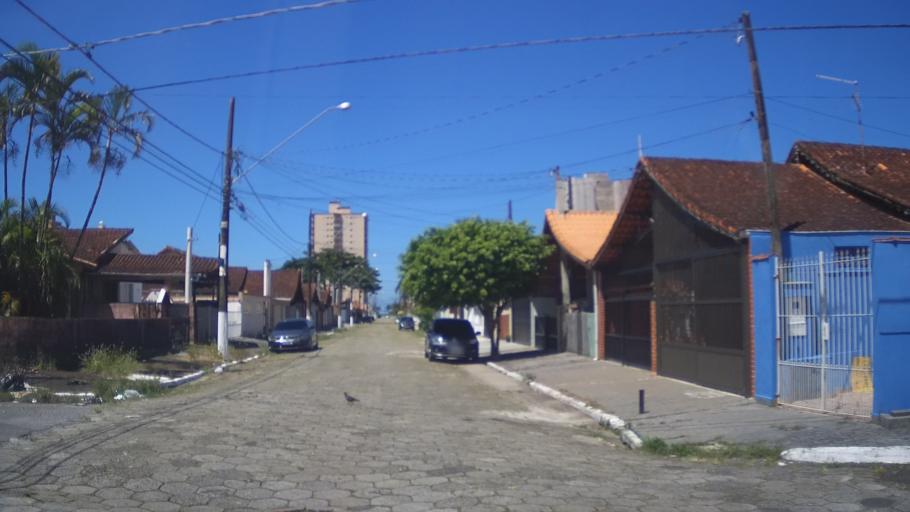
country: BR
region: Sao Paulo
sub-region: Mongagua
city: Mongagua
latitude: -24.0444
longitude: -46.5188
